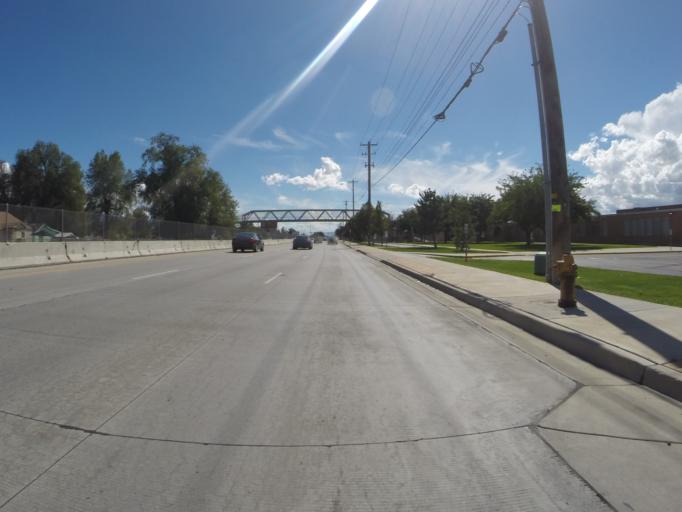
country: US
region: Utah
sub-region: Salt Lake County
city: Taylorsville
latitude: 40.7144
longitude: -111.9391
